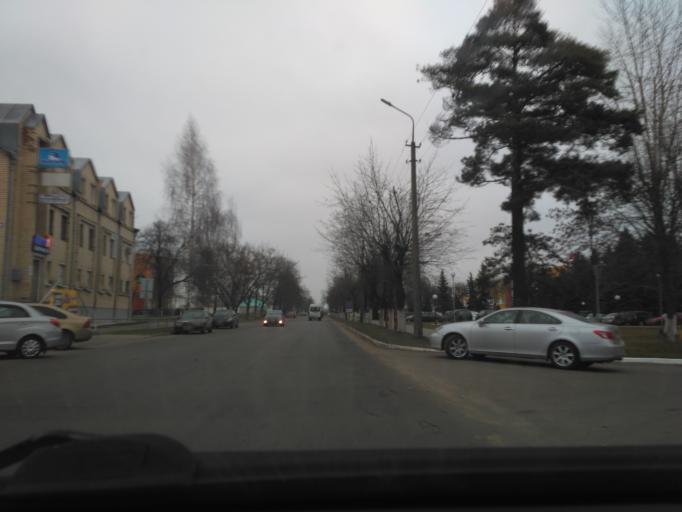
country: BY
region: Minsk
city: Horad Barysaw
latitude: 54.2094
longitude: 28.4893
